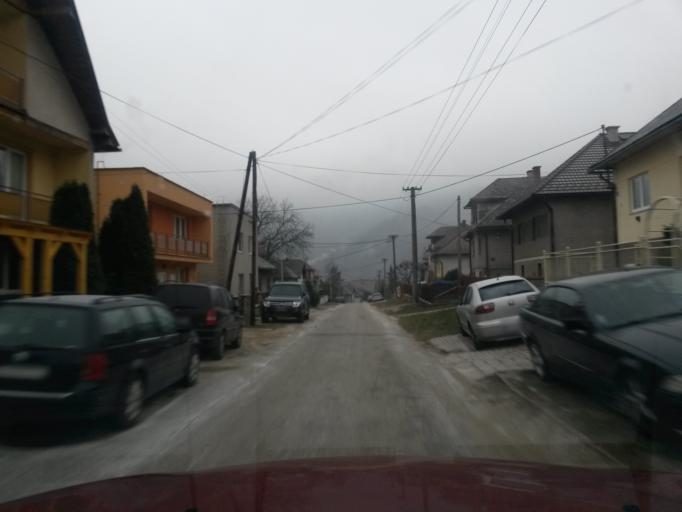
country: SK
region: Kosicky
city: Roznava
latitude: 48.7040
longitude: 20.5055
